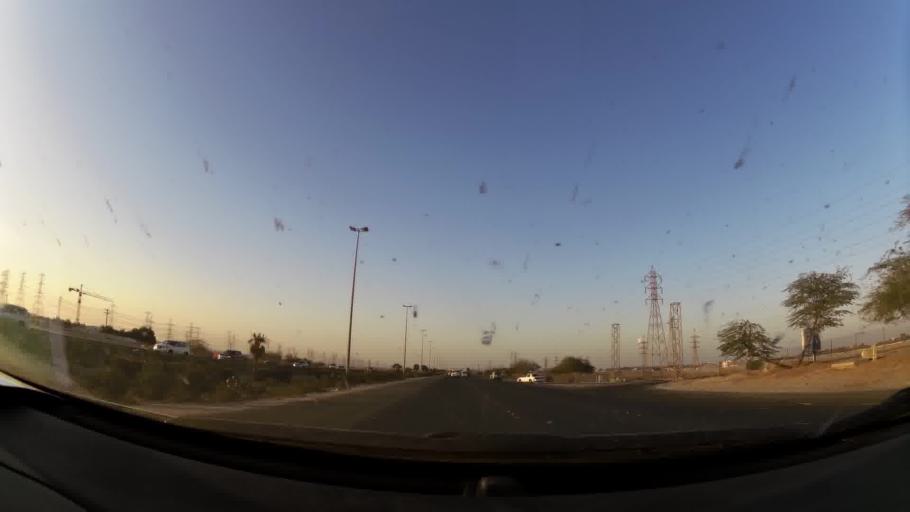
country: KW
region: Al Ahmadi
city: Al Fahahil
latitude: 28.8909
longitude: 48.2240
